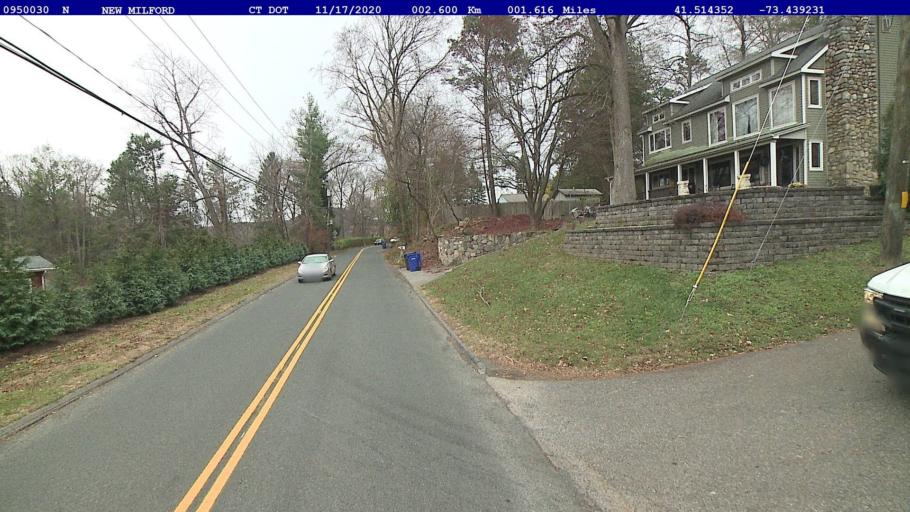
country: US
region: Connecticut
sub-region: Litchfield County
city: New Milford
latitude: 41.5144
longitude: -73.4393
